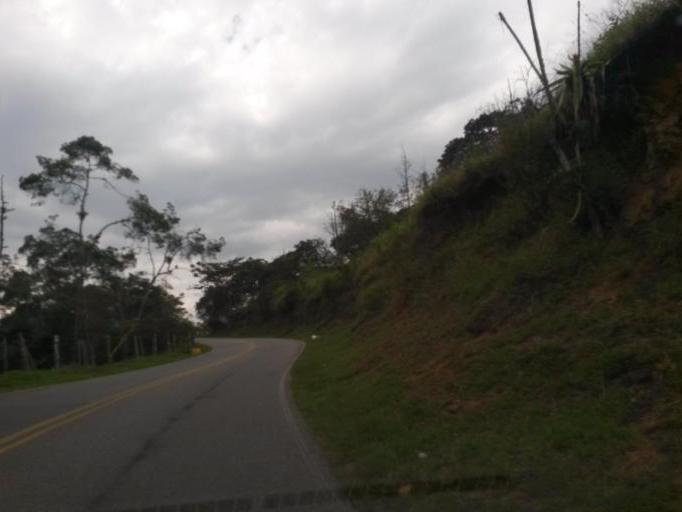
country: CO
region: Cauca
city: Lopez
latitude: 2.4434
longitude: -76.7401
